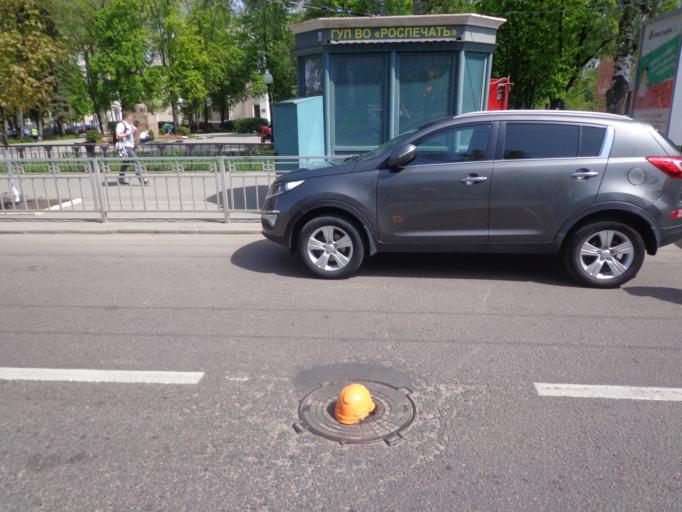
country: RU
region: Voronezj
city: Voronezh
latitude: 51.6595
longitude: 39.2028
